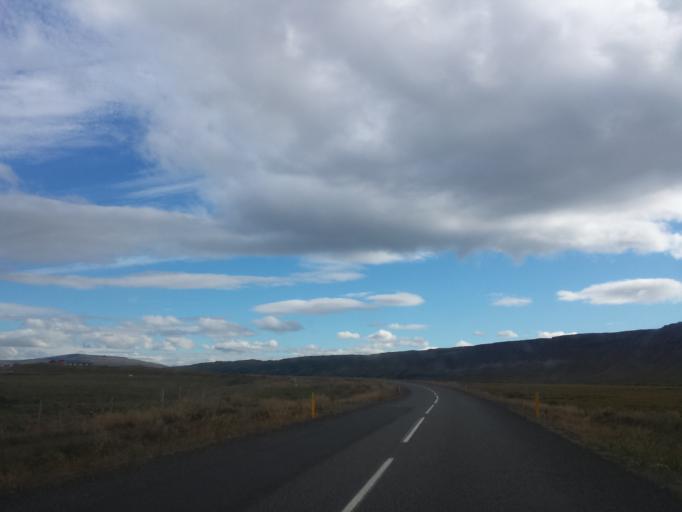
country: IS
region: West
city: Borgarnes
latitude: 64.4226
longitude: -21.7671
